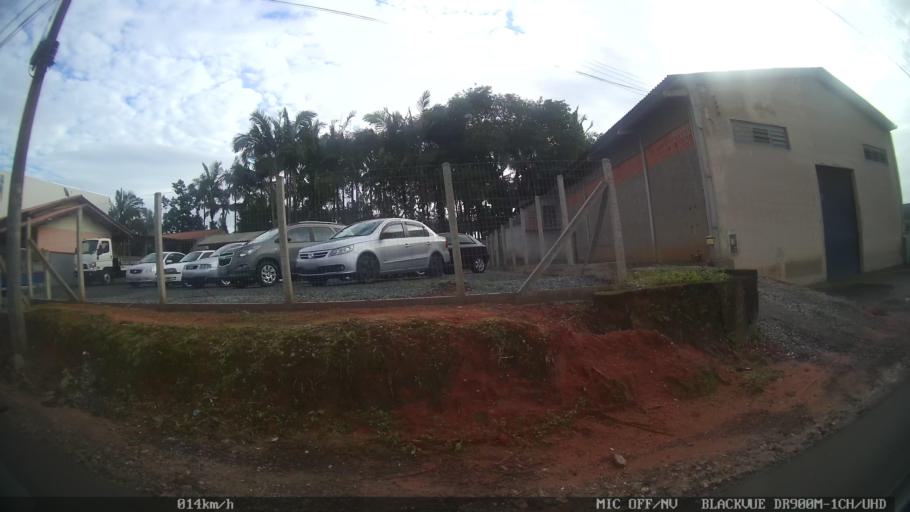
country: BR
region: Santa Catarina
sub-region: Barra Velha
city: Barra Velha
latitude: -26.6202
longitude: -48.7144
